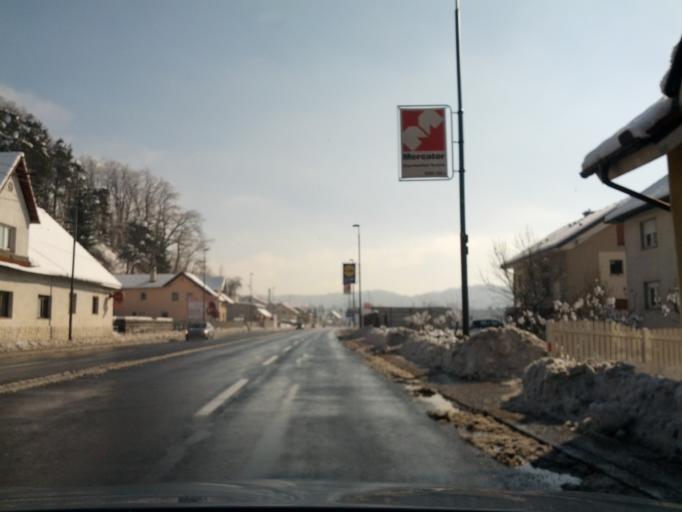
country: SI
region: Skofljica
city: Lavrica
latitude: 46.0275
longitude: 14.5363
